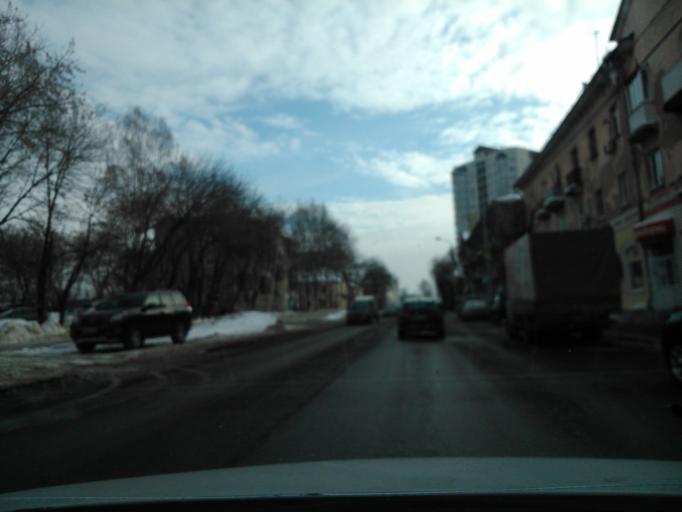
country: RU
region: Perm
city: Perm
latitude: 58.0010
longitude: 56.2398
